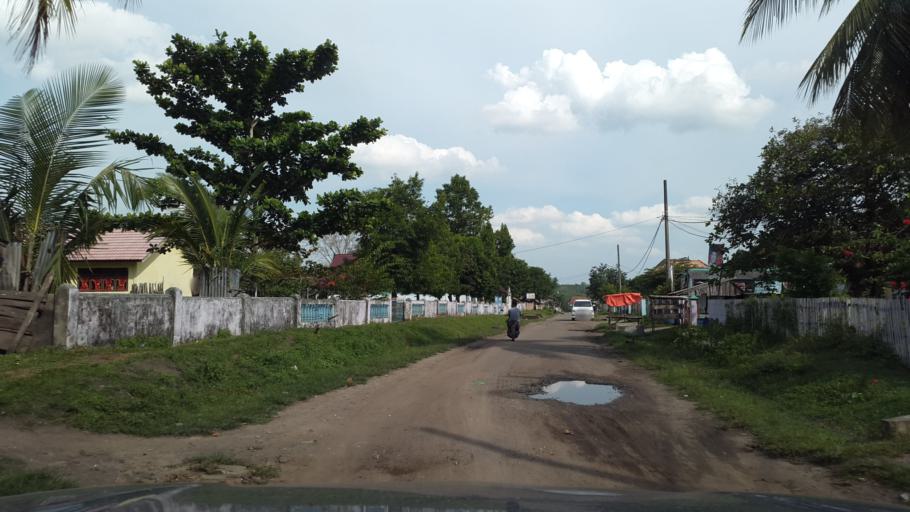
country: ID
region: South Sumatra
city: Prabumulih
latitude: -3.4371
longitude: 104.4058
